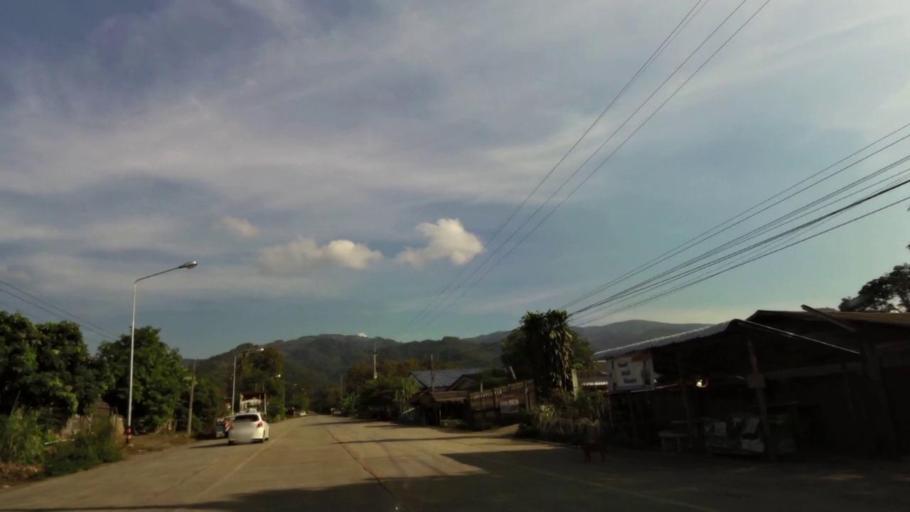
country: TH
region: Chiang Rai
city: Khun Tan
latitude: 19.8842
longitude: 100.2928
